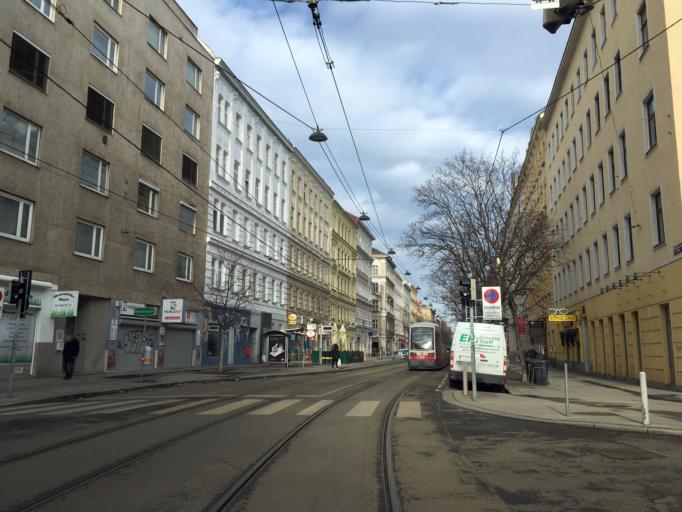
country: AT
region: Vienna
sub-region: Wien Stadt
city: Vienna
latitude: 48.2317
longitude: 16.3663
